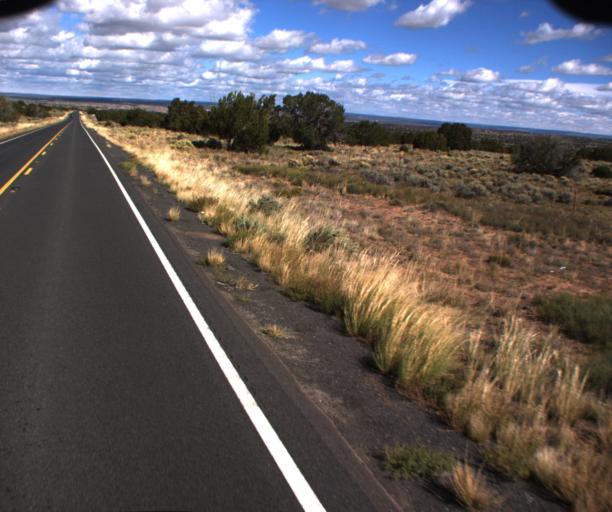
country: US
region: Arizona
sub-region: Apache County
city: Houck
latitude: 35.1445
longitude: -109.3332
